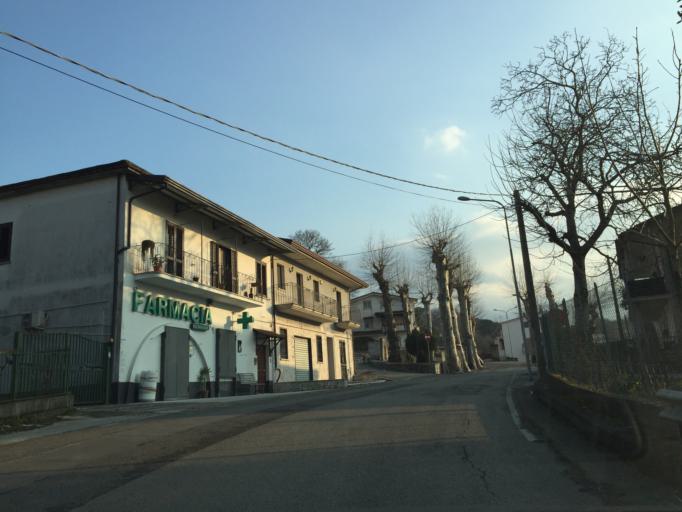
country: IT
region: Campania
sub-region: Provincia di Benevento
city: Arpaise
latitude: 41.0310
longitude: 14.7457
